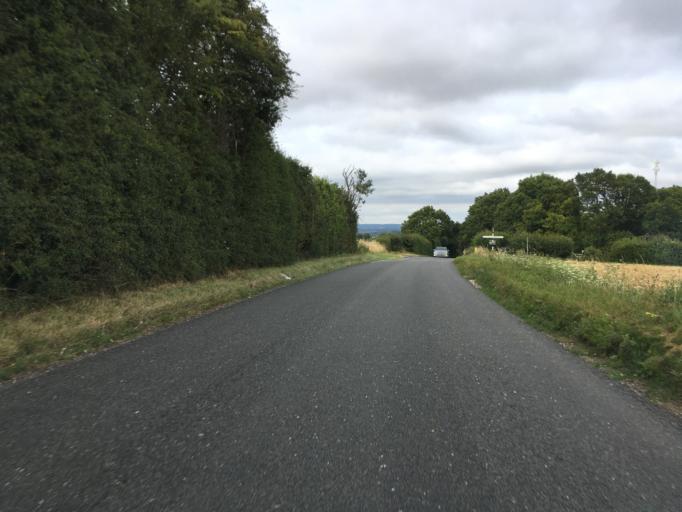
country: GB
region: England
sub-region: Hampshire
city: Bishops Waltham
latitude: 51.0329
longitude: -1.2159
